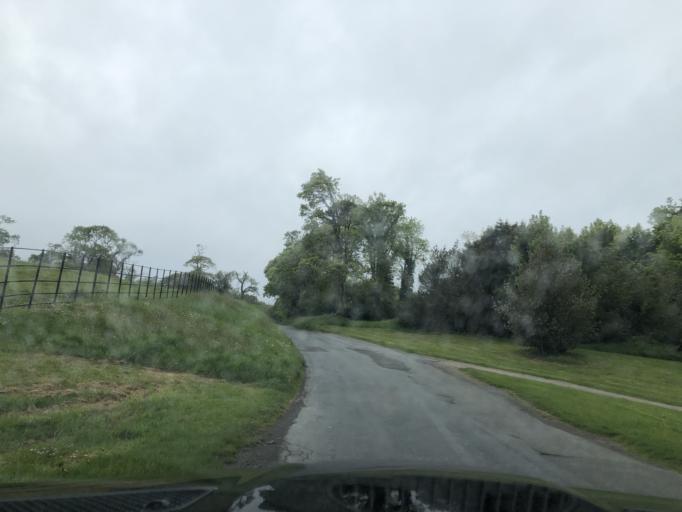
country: GB
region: Northern Ireland
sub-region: Down District
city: Portaferry
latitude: 54.3659
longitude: -5.5827
